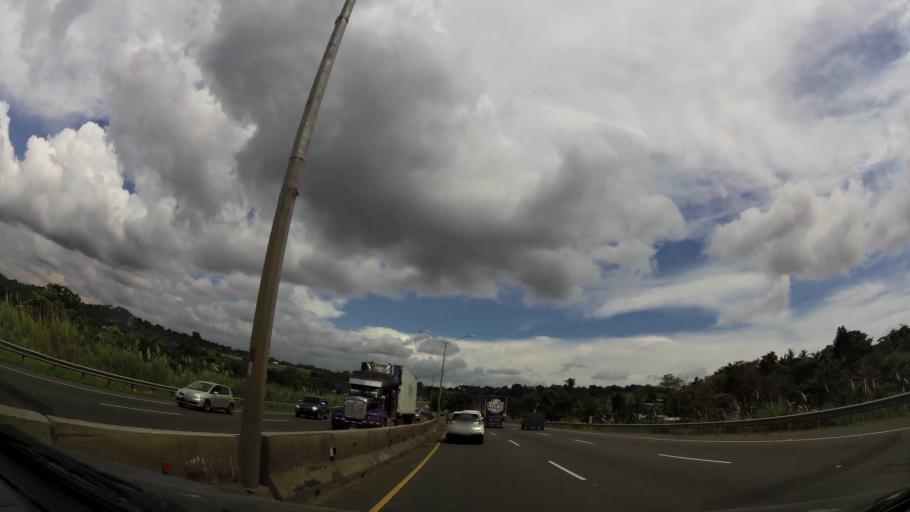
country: PA
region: Panama
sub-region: Distrito Arraijan
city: Arraijan
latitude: 8.9456
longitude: -79.6675
